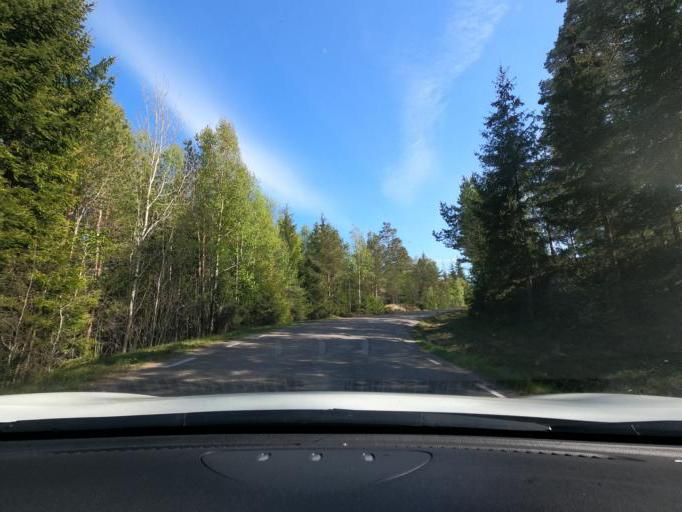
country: SE
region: Vaestra Goetaland
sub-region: Harryda Kommun
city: Hindas
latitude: 57.6678
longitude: 12.3536
